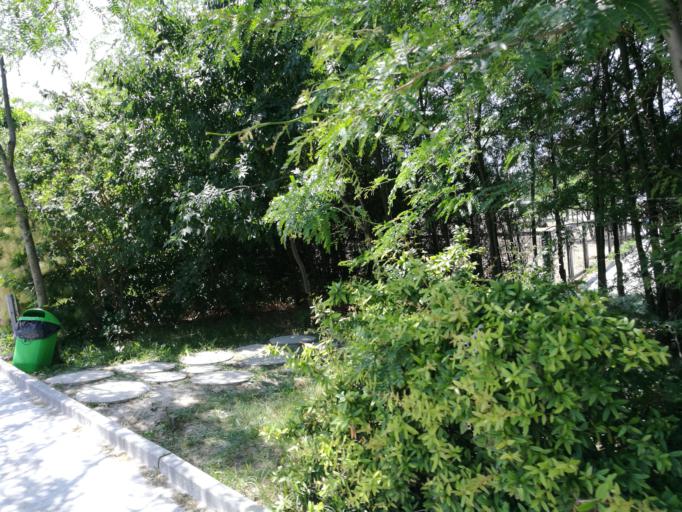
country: RO
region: Constanta
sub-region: Municipiul Constanta
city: Constanta
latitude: 44.2052
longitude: 28.6401
